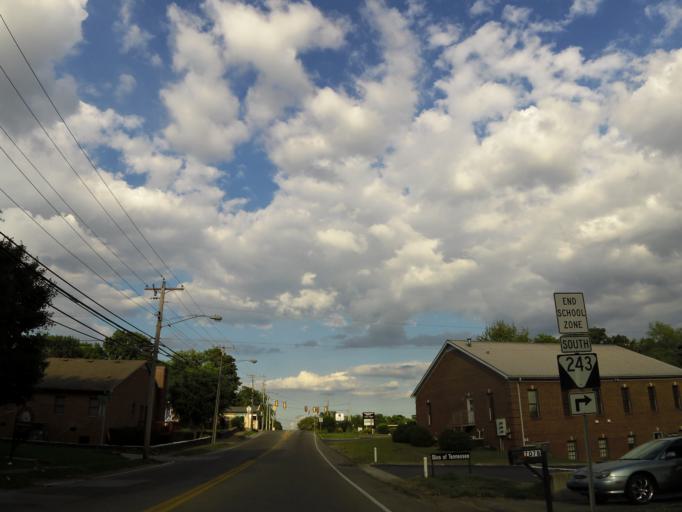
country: US
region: Tennessee
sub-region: Maury County
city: Columbia
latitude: 35.6161
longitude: -87.0472
